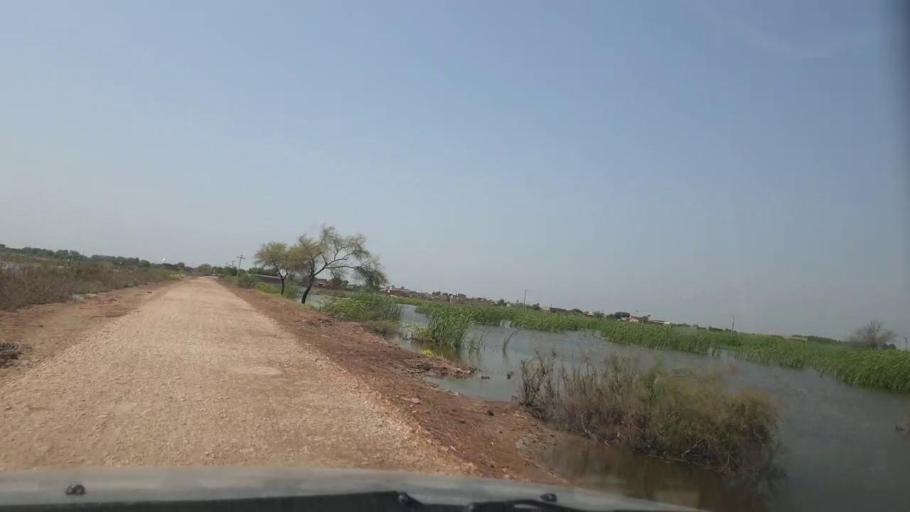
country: PK
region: Sindh
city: Tando Ghulam Ali
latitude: 25.1141
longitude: 68.7903
